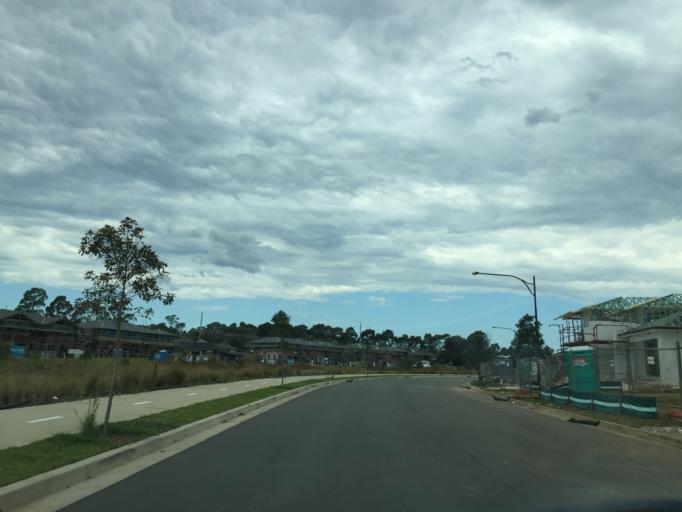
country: AU
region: New South Wales
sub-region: Blacktown
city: Doonside
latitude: -33.7771
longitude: 150.8704
